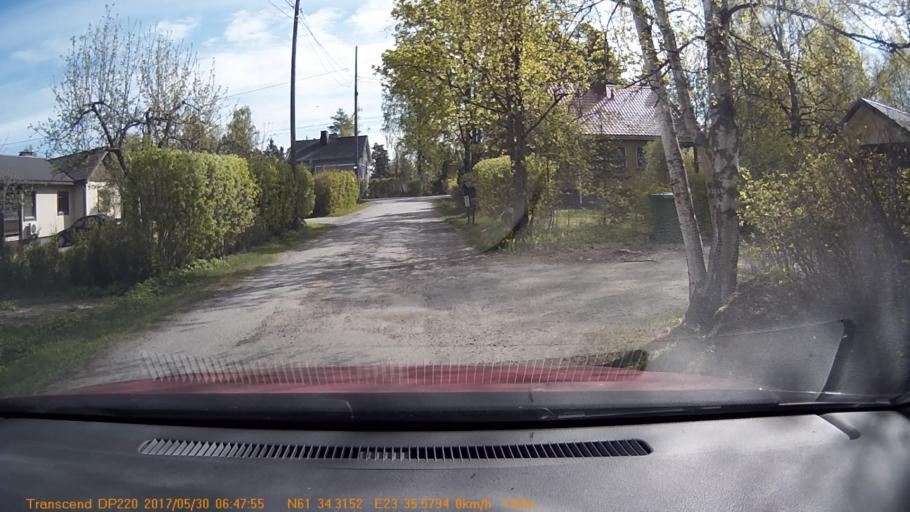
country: FI
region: Pirkanmaa
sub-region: Tampere
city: Yloejaervi
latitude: 61.5719
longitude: 23.5929
